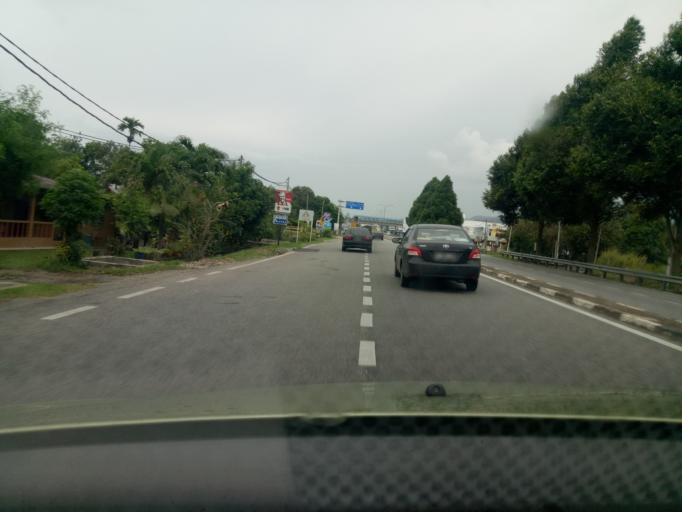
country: MY
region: Kedah
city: Gurun
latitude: 5.8621
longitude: 100.4557
